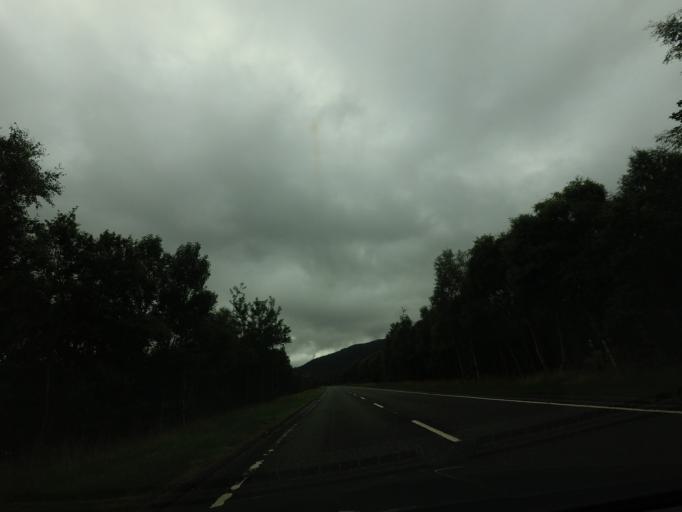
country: GB
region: Scotland
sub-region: Highland
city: Aviemore
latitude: 57.2014
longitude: -3.8338
